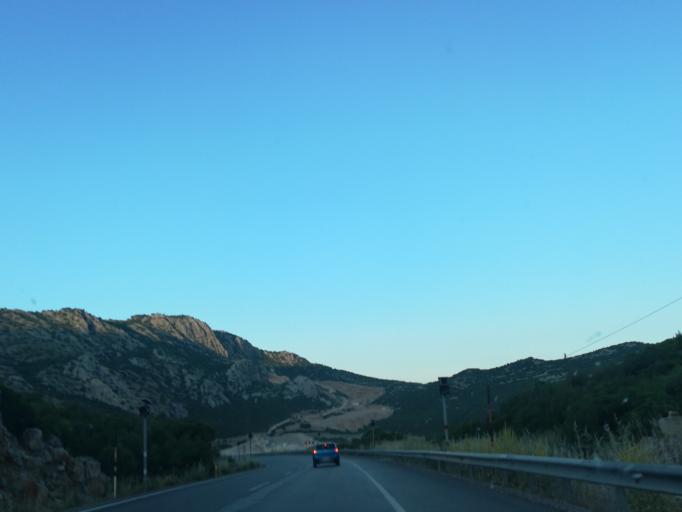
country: TR
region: Antalya
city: Dagbeli
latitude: 37.1548
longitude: 30.5039
